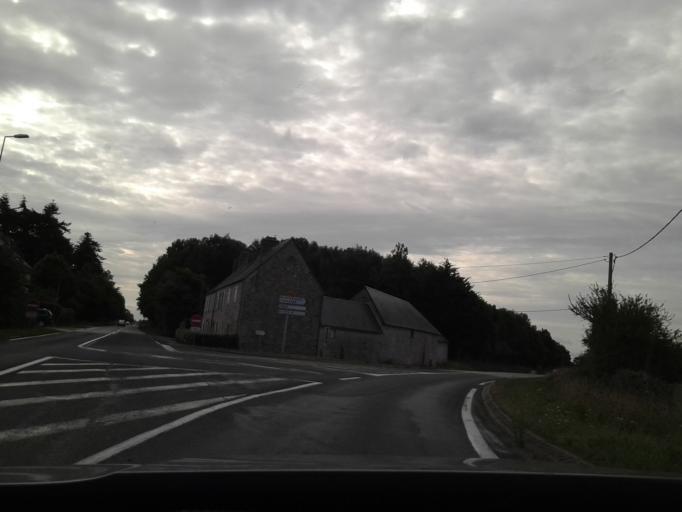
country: FR
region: Lower Normandy
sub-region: Departement de la Manche
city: Valognes
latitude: 49.5006
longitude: -1.4531
